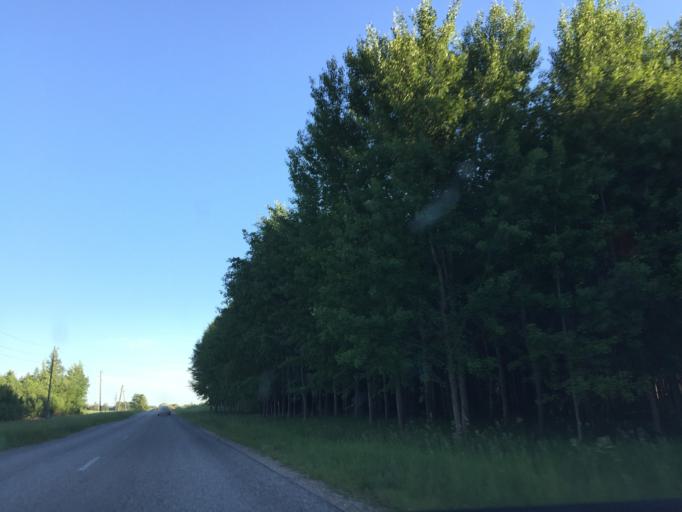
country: LV
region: Broceni
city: Broceni
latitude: 56.6983
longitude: 22.5054
